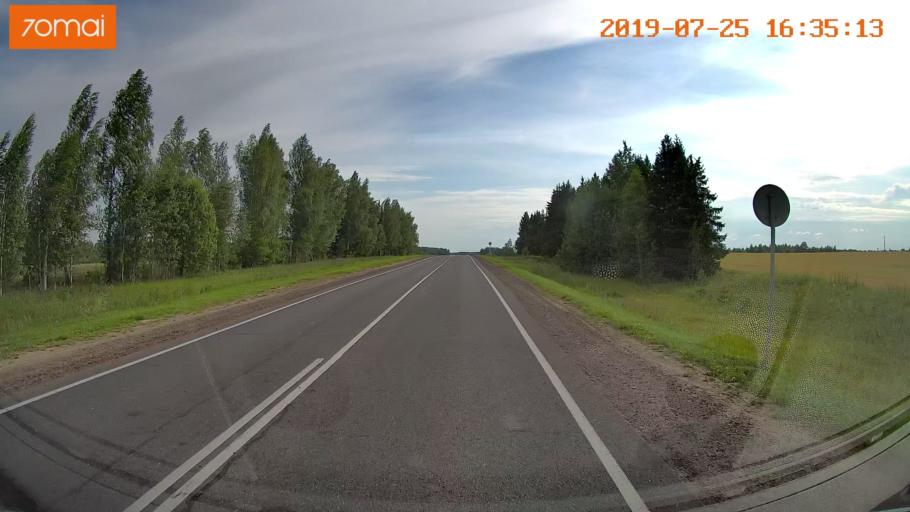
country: RU
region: Ivanovo
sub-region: Privolzhskiy Rayon
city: Ples
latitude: 57.4081
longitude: 41.4239
